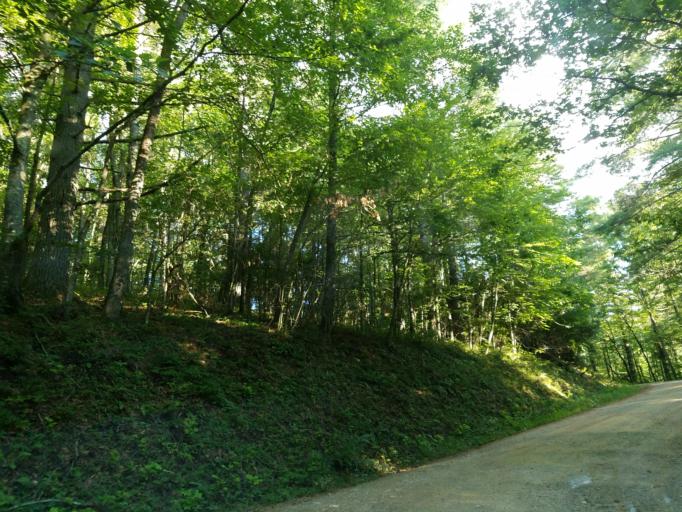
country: US
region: Georgia
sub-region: Union County
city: Blairsville
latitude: 34.7496
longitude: -84.0698
